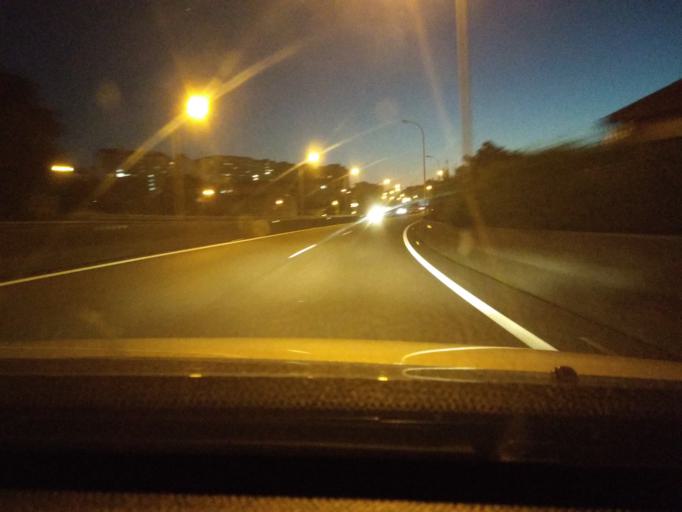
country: ES
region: Galicia
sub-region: Provincia de Pontevedra
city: Vigo
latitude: 42.2464
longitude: -8.6965
